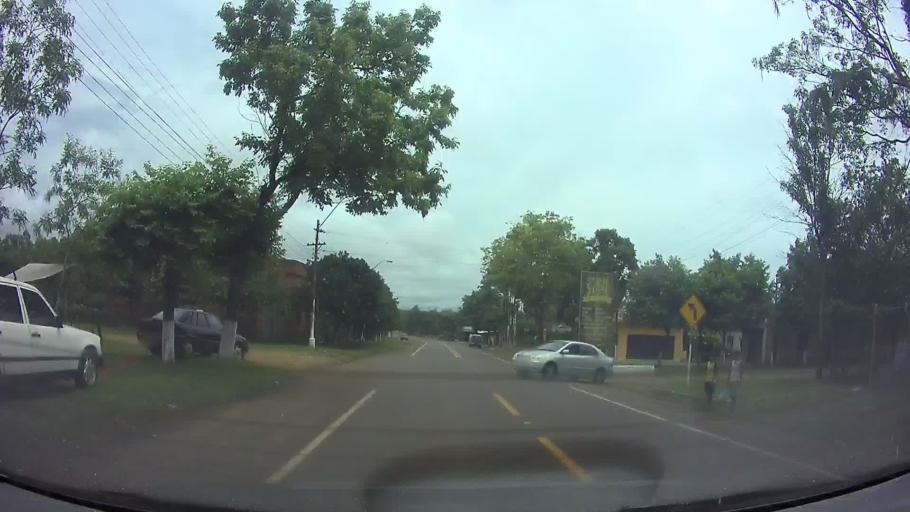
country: PY
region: Paraguari
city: Acahay
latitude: -25.9082
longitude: -57.1145
